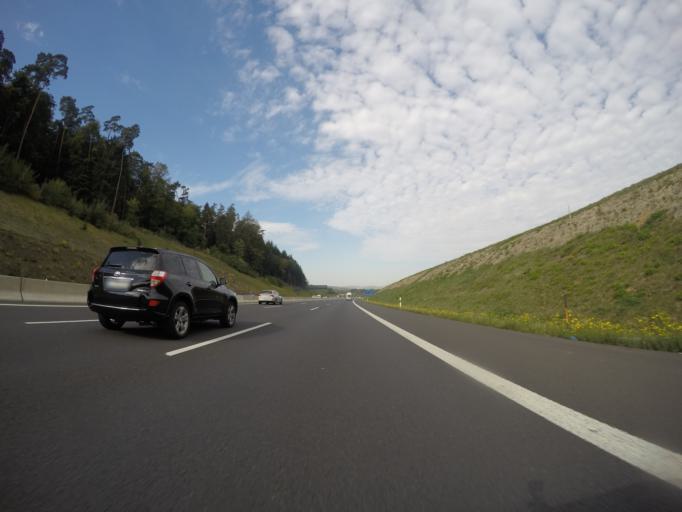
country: DE
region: Bavaria
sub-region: Regierungsbezirk Unterfranken
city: Waldaschaff
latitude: 49.9796
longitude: 9.2692
